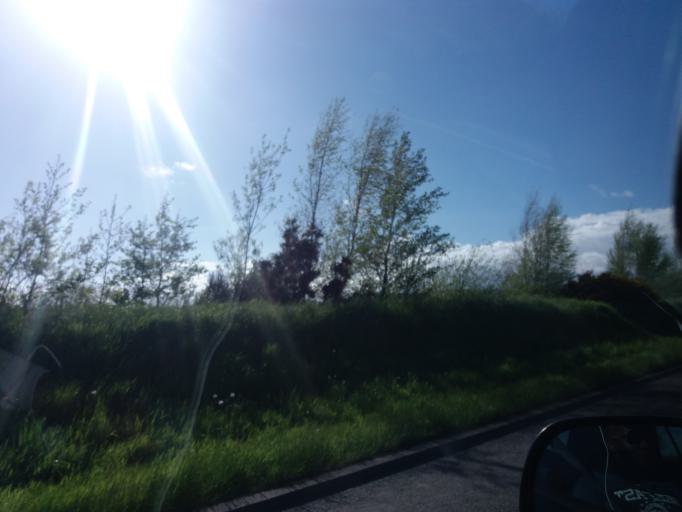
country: IE
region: Munster
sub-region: Waterford
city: Waterford
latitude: 52.3342
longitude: -7.1580
